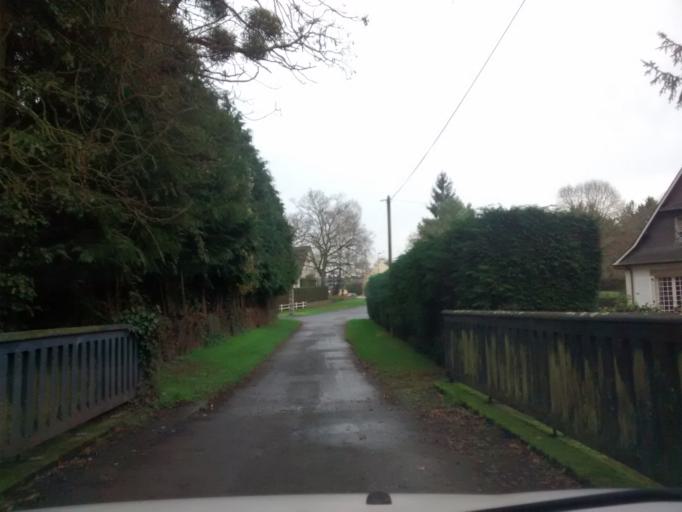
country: FR
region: Brittany
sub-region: Departement d'Ille-et-Vilaine
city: Acigne
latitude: 48.1300
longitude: -1.5450
